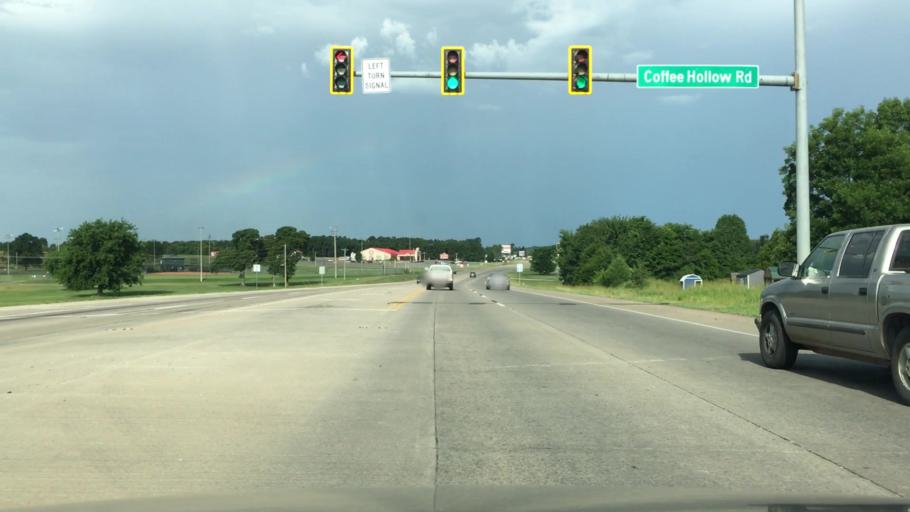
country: US
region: Oklahoma
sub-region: Cherokee County
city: Park Hill
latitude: 35.8497
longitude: -95.0032
